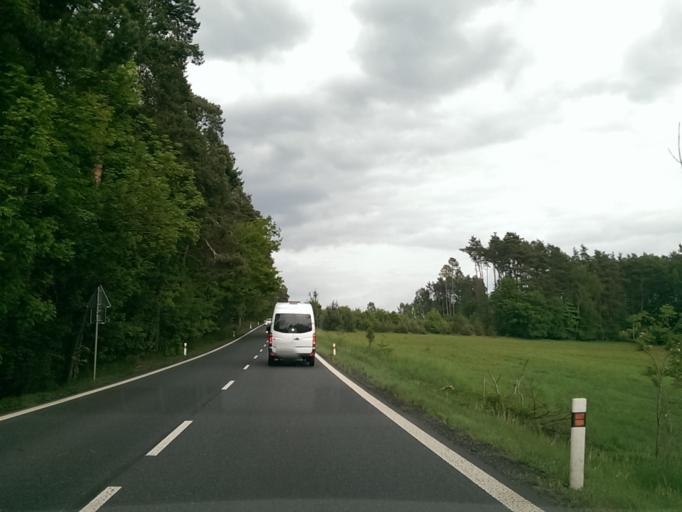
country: CZ
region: Central Bohemia
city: Bela pod Bezdezem
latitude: 50.5186
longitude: 14.7390
